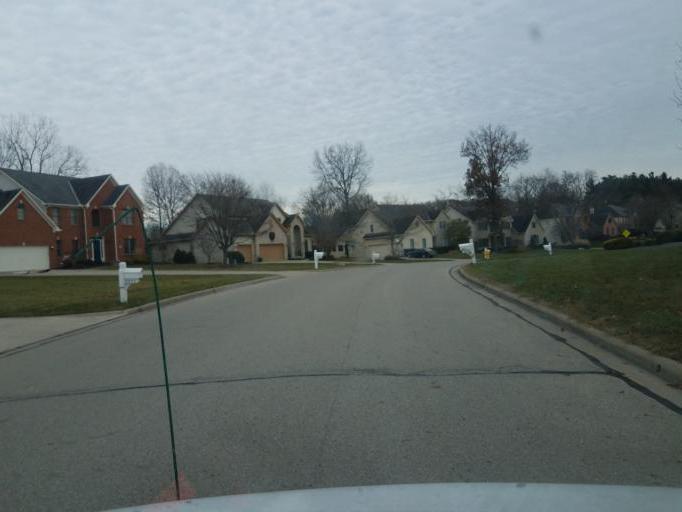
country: US
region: Ohio
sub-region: Franklin County
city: Westerville
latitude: 40.1793
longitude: -82.9419
